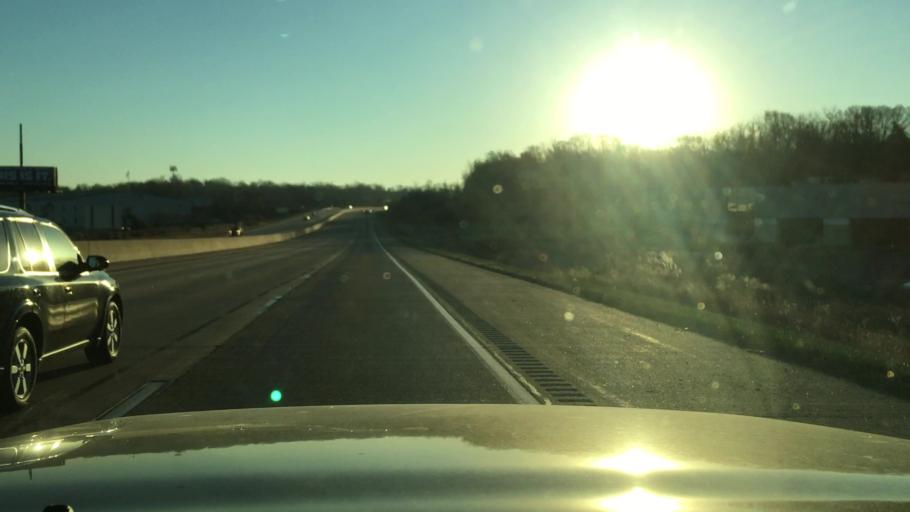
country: US
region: Missouri
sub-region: Saint Charles County
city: Saint Charles
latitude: 38.8204
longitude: -90.5048
